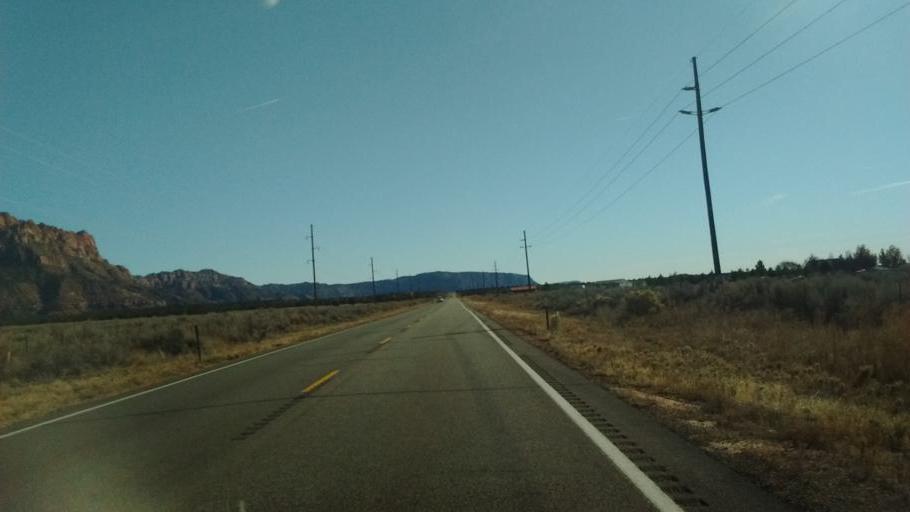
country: US
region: Arizona
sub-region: Mohave County
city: Colorado City
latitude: 37.0294
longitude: -113.0541
